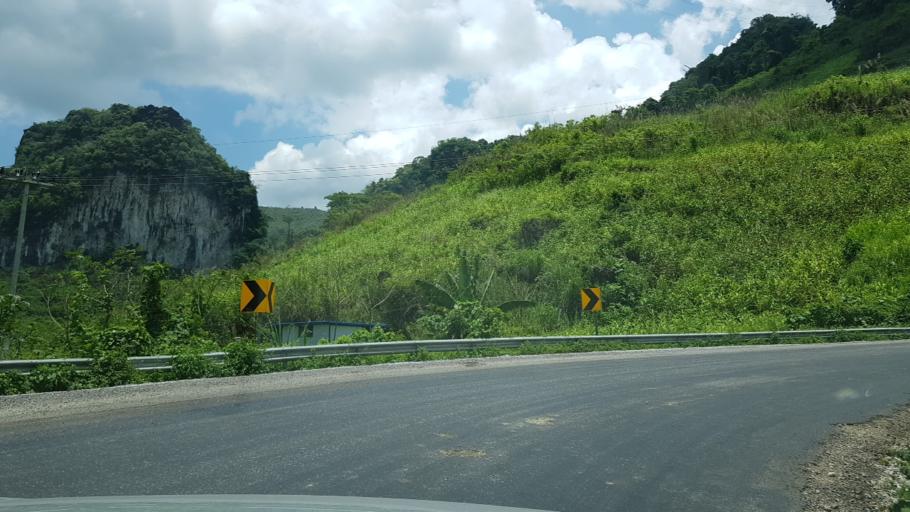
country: LA
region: Vientiane
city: Muang Kasi
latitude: 19.1413
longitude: 102.2912
